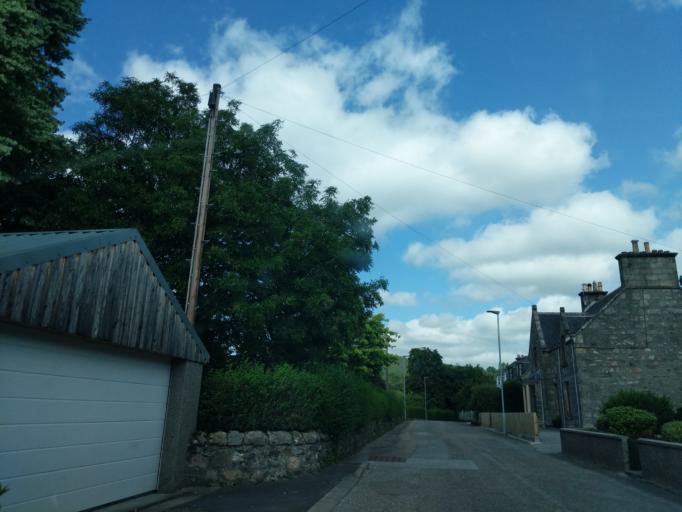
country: GB
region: Scotland
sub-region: Moray
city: Rothes
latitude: 57.4904
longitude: -3.1865
